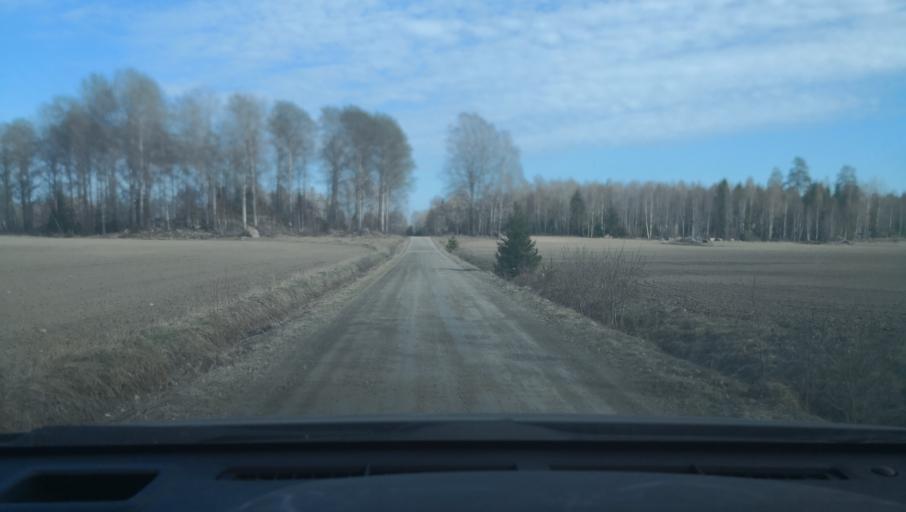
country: SE
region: Uppsala
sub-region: Heby Kommun
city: Heby
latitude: 59.8389
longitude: 16.8953
